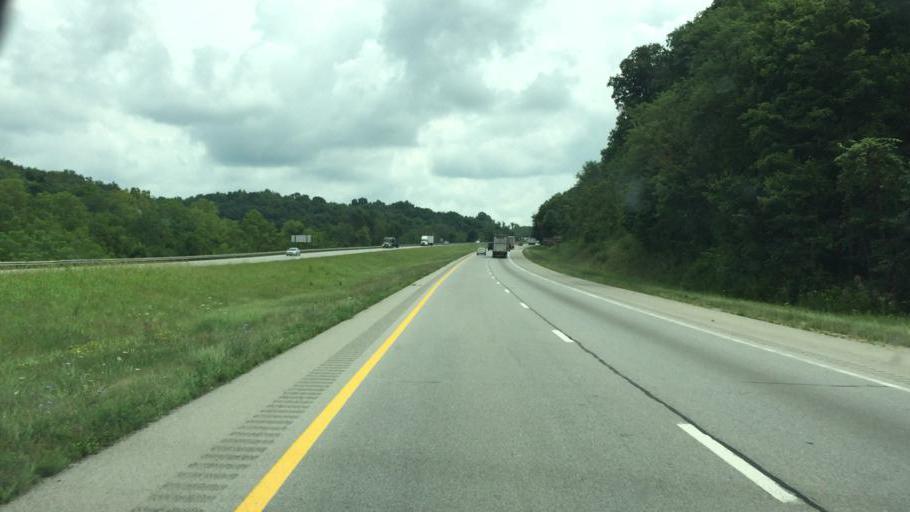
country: US
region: Ohio
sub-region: Guernsey County
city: Byesville
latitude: 40.0275
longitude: -81.4654
